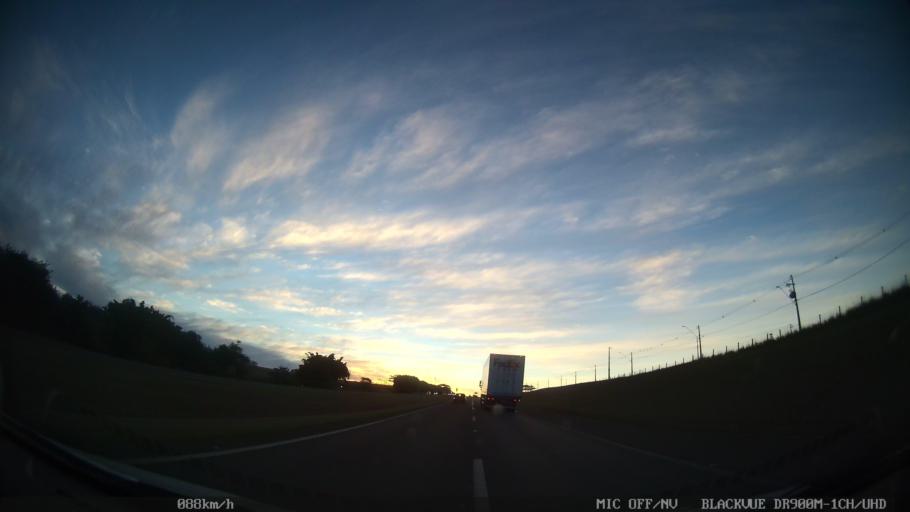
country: BR
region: Sao Paulo
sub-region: Catanduva
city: Catanduva
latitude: -21.1398
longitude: -49.0125
